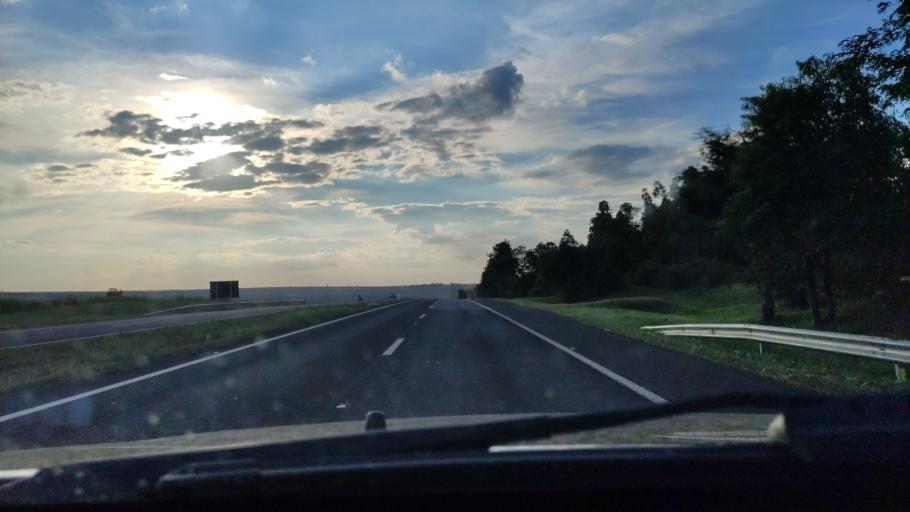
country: BR
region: Sao Paulo
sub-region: Rancharia
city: Rancharia
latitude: -22.4275
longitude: -51.0217
